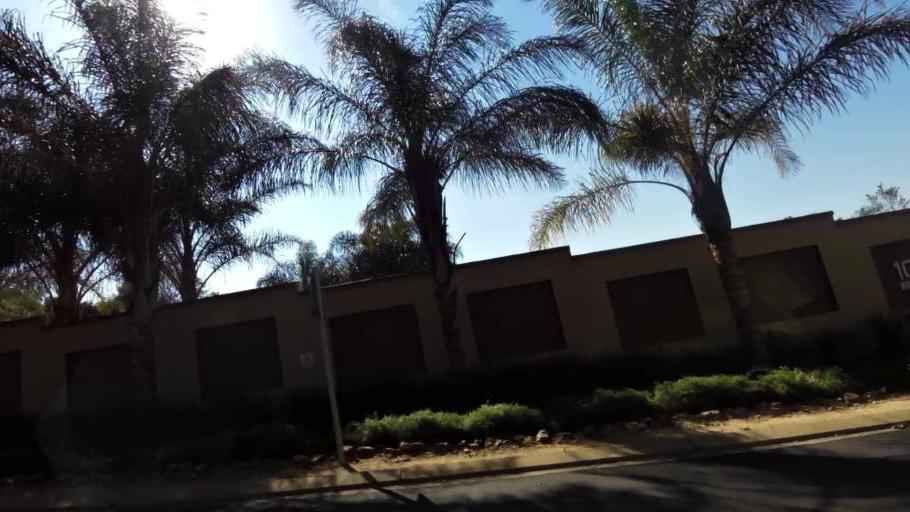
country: ZA
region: Gauteng
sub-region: City of Johannesburg Metropolitan Municipality
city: Roodepoort
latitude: -26.1419
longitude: 27.9428
